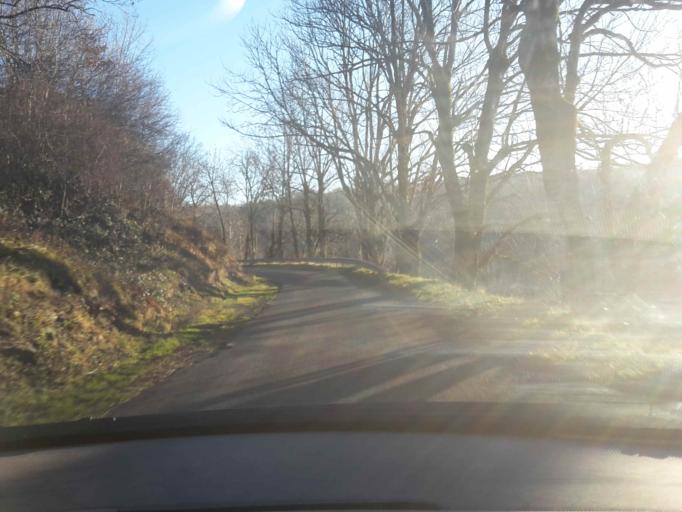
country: FR
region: Auvergne
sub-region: Departement du Cantal
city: Ydes
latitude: 45.2404
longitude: 2.5425
